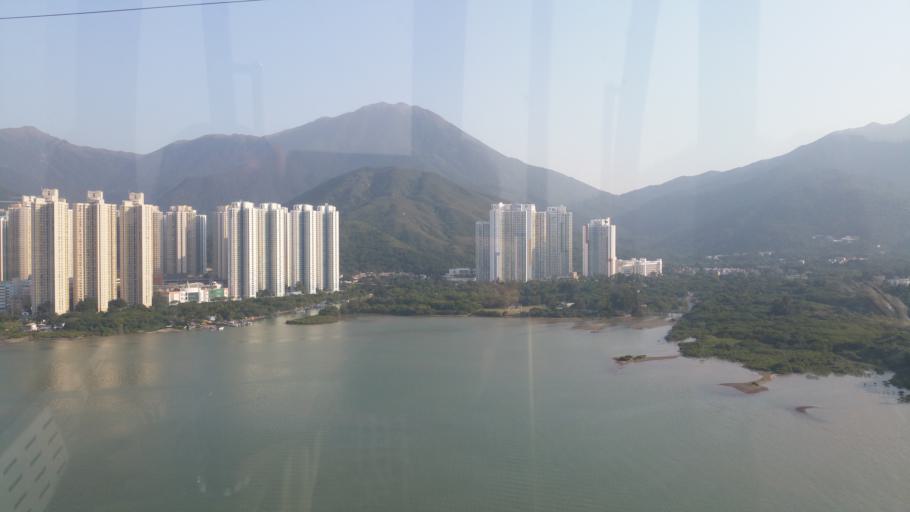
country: HK
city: Tai O
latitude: 22.2869
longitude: 113.9275
